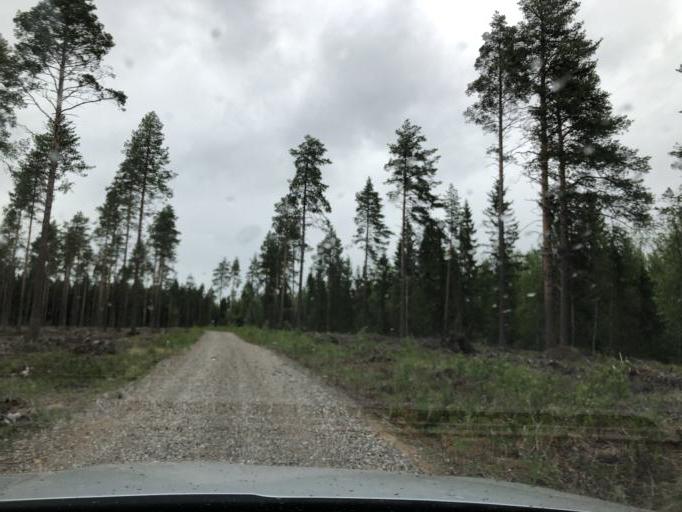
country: SE
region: Norrbotten
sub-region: Pitea Kommun
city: Roknas
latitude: 65.3977
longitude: 21.2701
